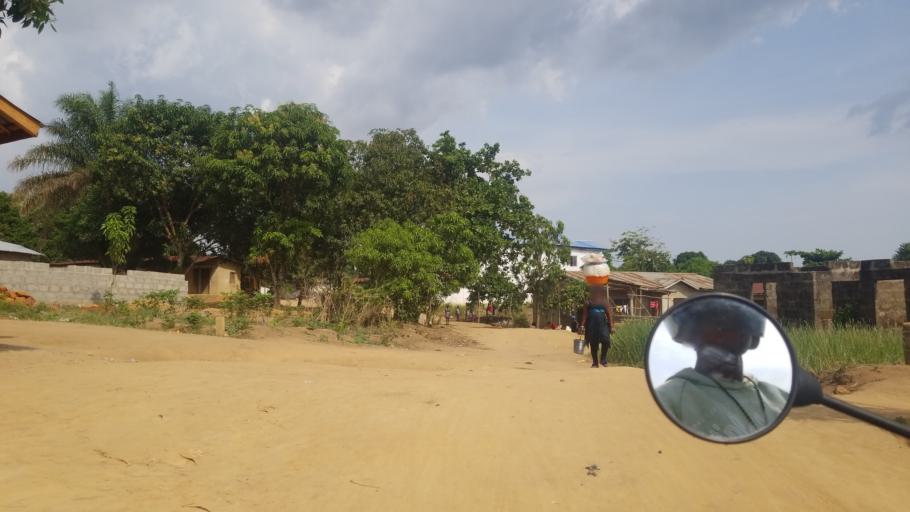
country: SL
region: Western Area
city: Waterloo
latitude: 8.3166
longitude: -13.0487
